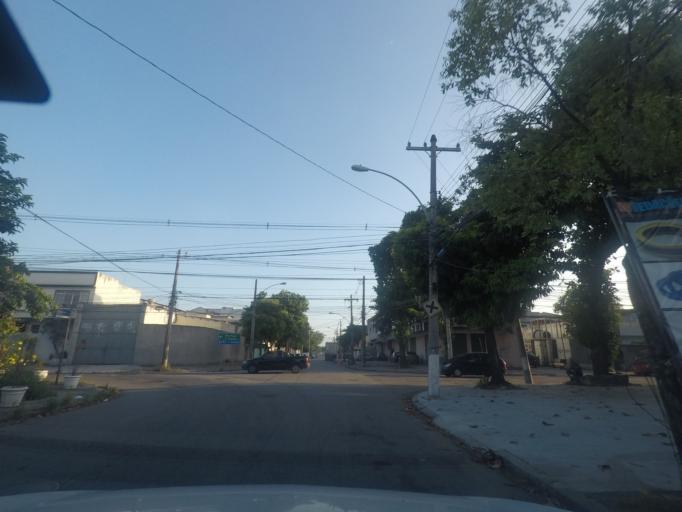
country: BR
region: Rio de Janeiro
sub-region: Duque De Caxias
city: Duque de Caxias
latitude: -22.8311
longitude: -43.2740
